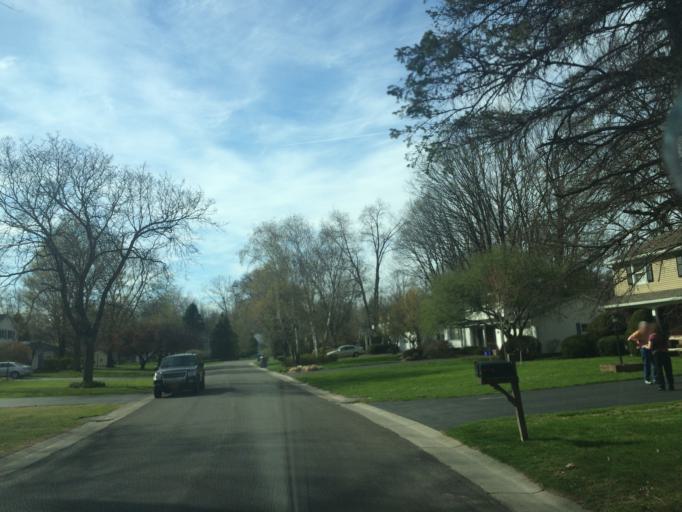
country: US
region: New York
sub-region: Monroe County
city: East Rochester
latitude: 43.0923
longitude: -77.4695
